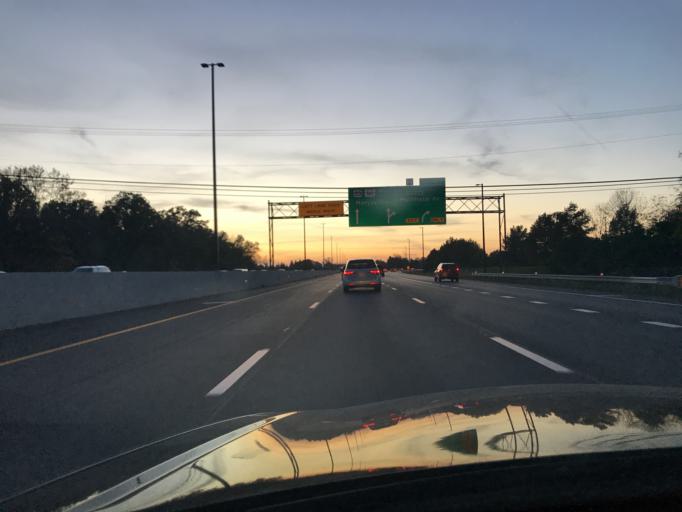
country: US
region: Ohio
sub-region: Franklin County
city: Dublin
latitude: 40.0993
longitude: -83.1510
